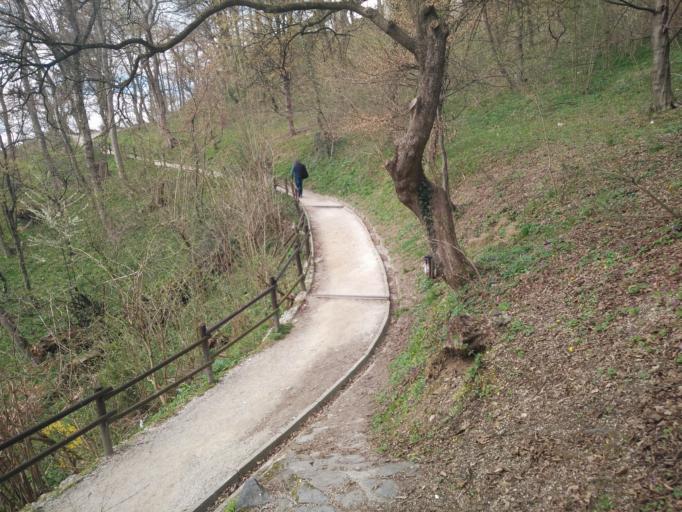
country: SI
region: Ljubljana
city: Ljubljana
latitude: 46.0477
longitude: 14.5083
